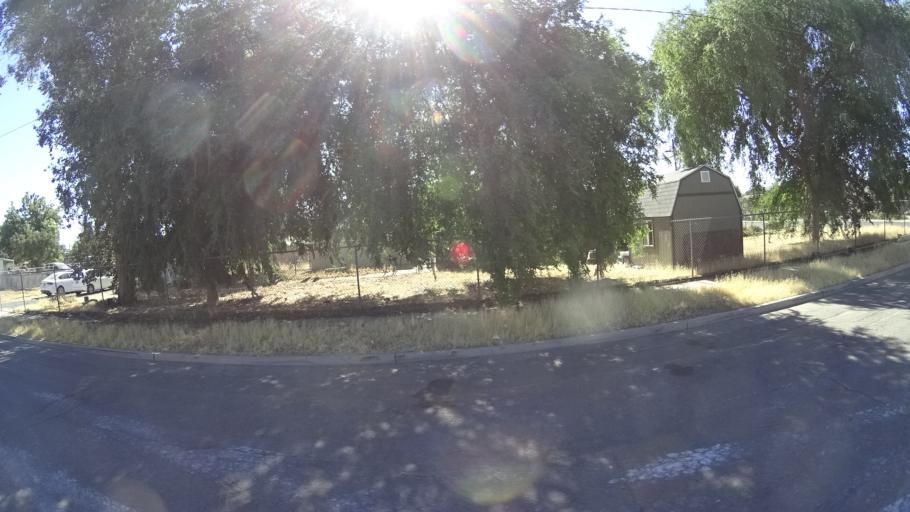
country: US
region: California
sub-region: Fresno County
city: West Park
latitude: 36.7597
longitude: -119.8400
